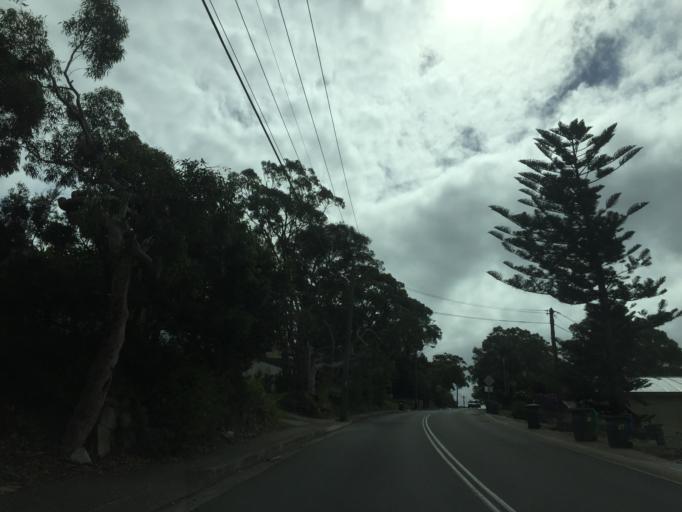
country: AU
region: New South Wales
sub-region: Pittwater
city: North Narrabeen
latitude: -33.7017
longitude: 151.2902
